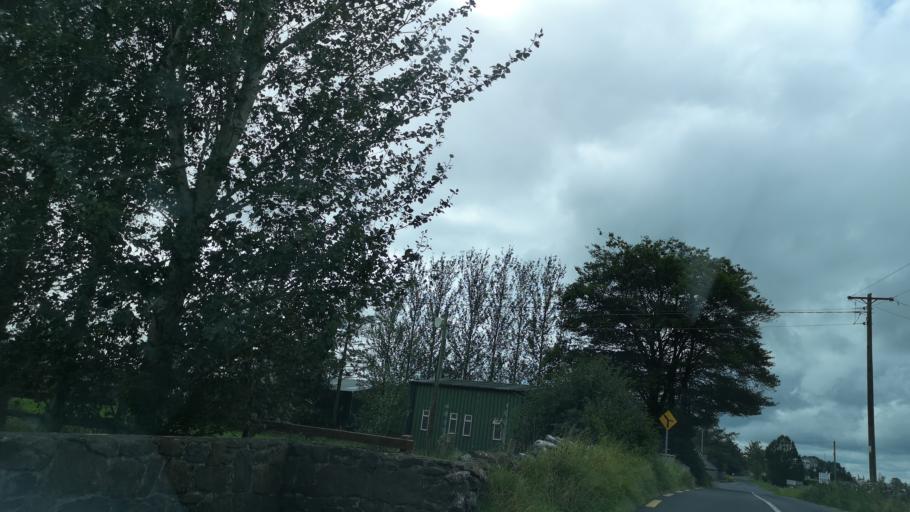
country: IE
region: Connaught
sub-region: County Galway
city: Loughrea
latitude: 53.2793
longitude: -8.6326
